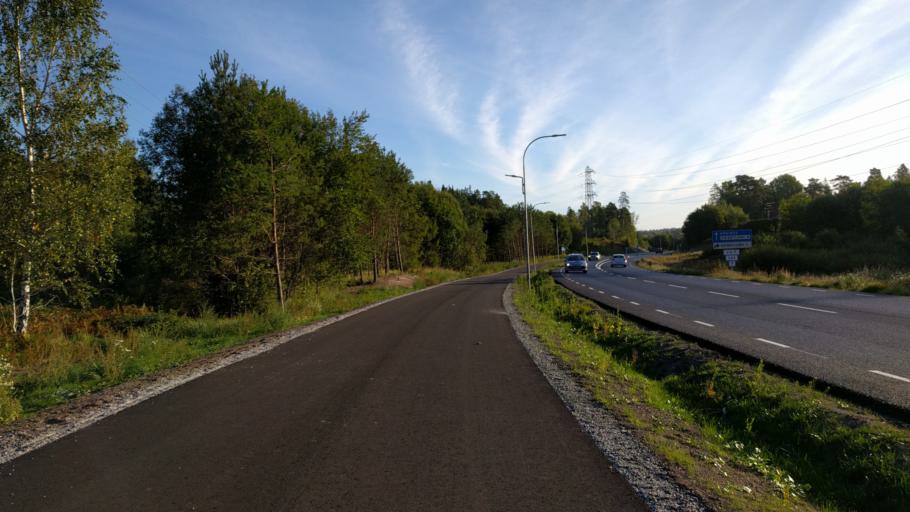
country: SE
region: Stockholm
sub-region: Taby Kommun
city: Taby
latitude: 59.4684
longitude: 18.0775
